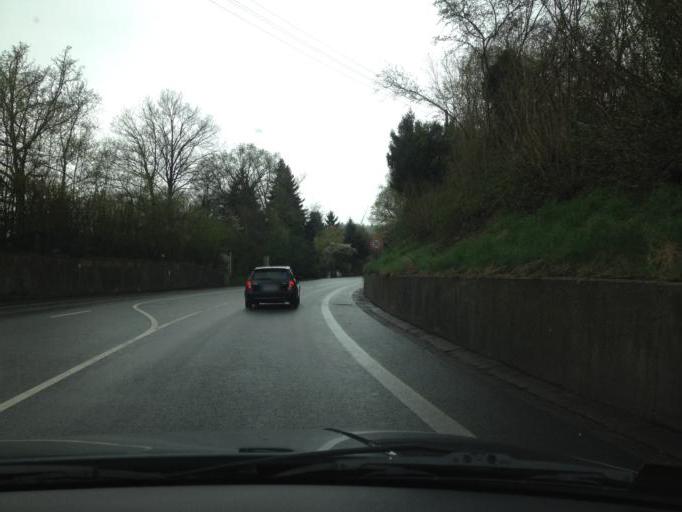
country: DE
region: Saarland
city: Ottweiler
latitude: 49.3973
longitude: 7.1660
